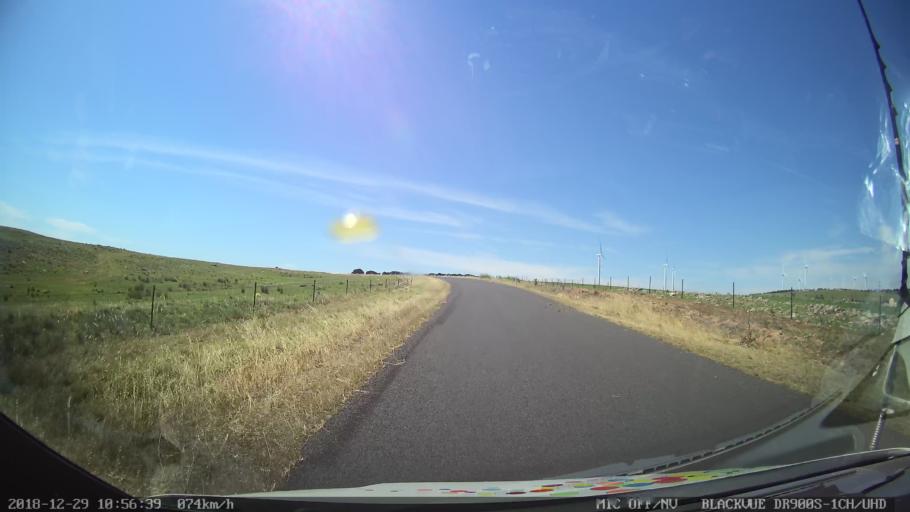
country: AU
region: New South Wales
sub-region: Palerang
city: Bungendore
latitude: -35.1365
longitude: 149.5395
